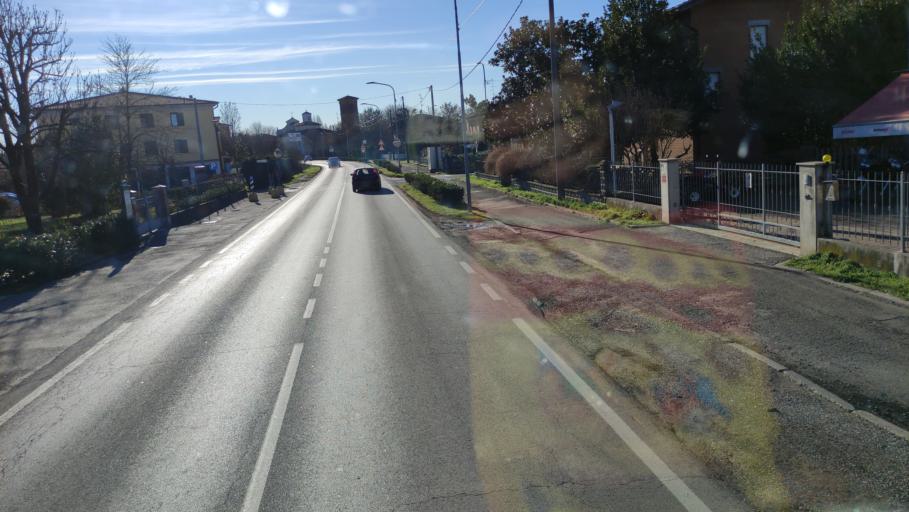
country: IT
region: Emilia-Romagna
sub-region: Provincia di Reggio Emilia
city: Novellara
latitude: 44.8512
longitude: 10.7338
